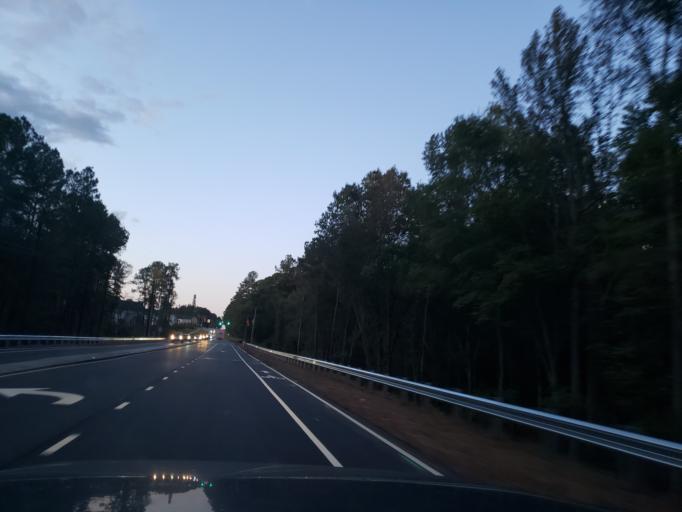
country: US
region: North Carolina
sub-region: Orange County
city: Chapel Hill
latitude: 35.8865
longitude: -78.9569
